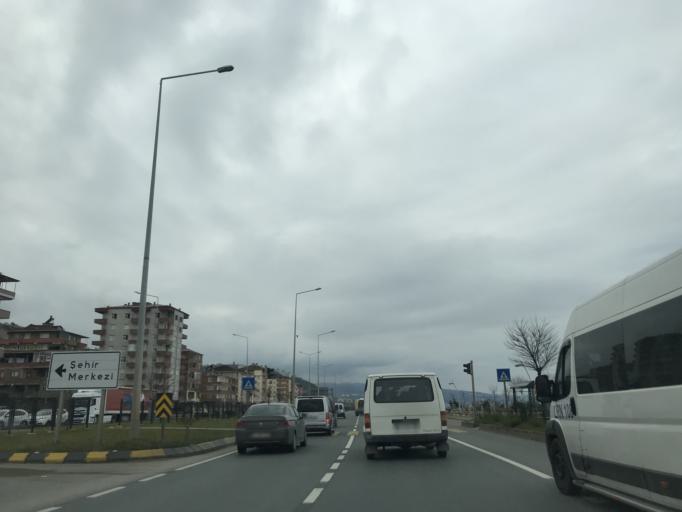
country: TR
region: Trabzon
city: Arsin
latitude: 40.9545
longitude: 39.9241
